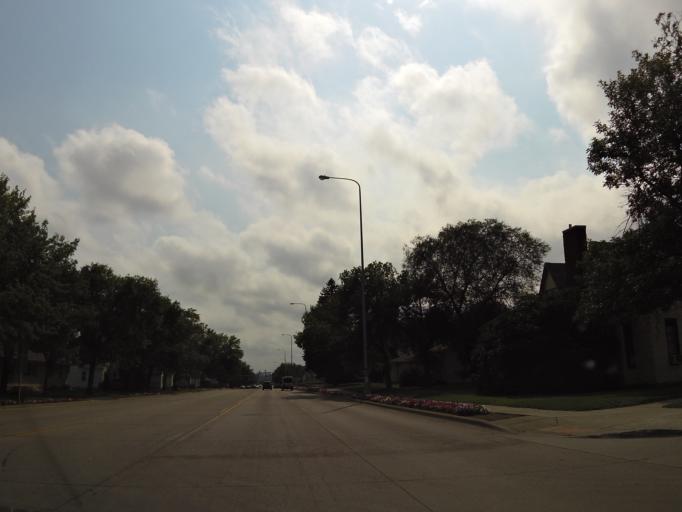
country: US
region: South Dakota
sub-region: Codington County
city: Watertown
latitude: 44.8966
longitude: -97.1074
